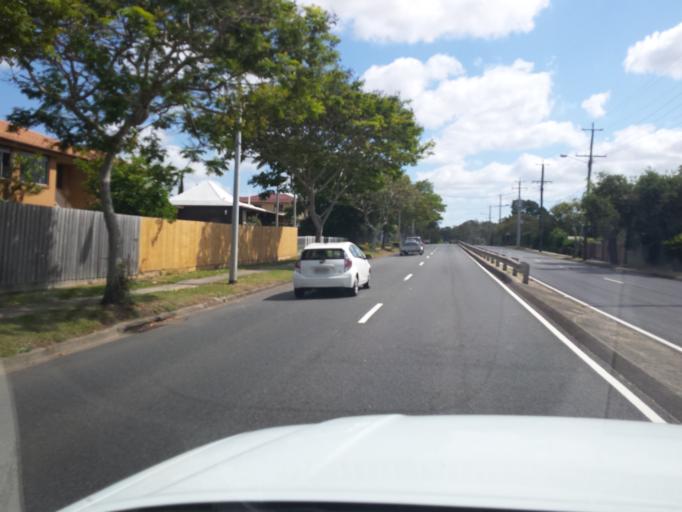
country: AU
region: Queensland
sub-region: Brisbane
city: Chermside West
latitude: -27.3786
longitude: 153.0230
